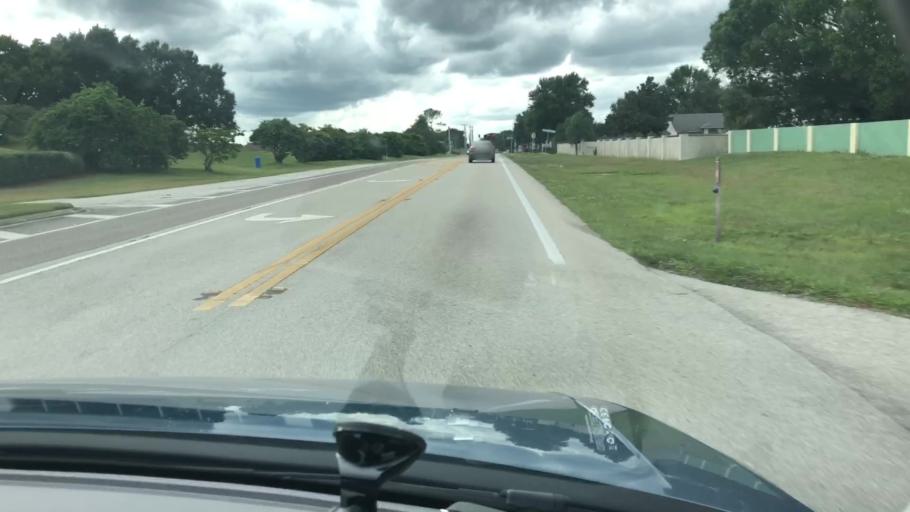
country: US
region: Florida
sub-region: Polk County
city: Kathleen
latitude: 28.1356
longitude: -82.0037
